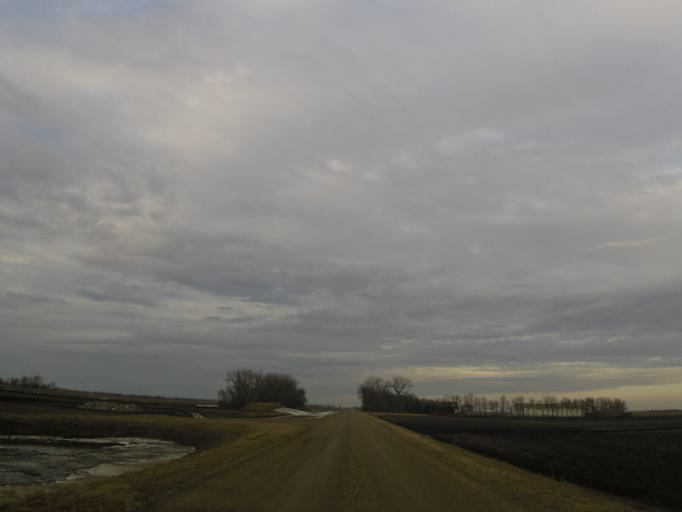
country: US
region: North Dakota
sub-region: Walsh County
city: Grafton
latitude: 48.3686
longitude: -97.2260
